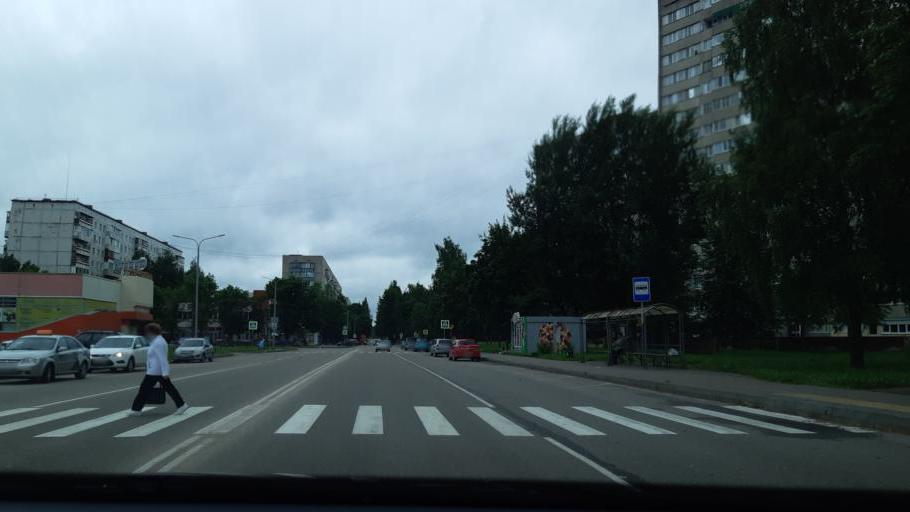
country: RU
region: Smolensk
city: Desnogorsk
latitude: 54.1530
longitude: 33.2880
